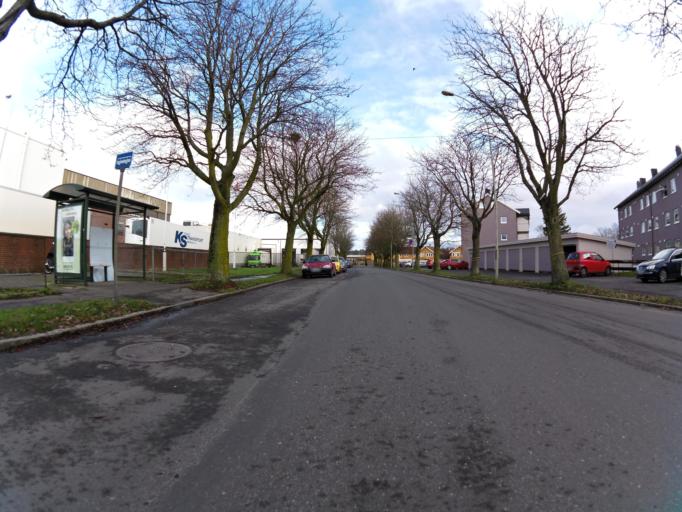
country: NO
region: Ostfold
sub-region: Sarpsborg
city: Sarpsborg
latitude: 59.2727
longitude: 11.0863
